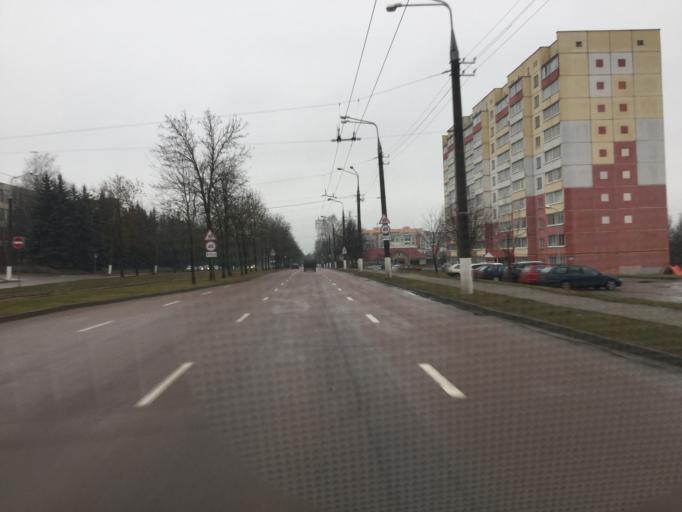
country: BY
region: Vitebsk
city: Vitebsk
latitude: 55.1968
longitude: 30.2602
